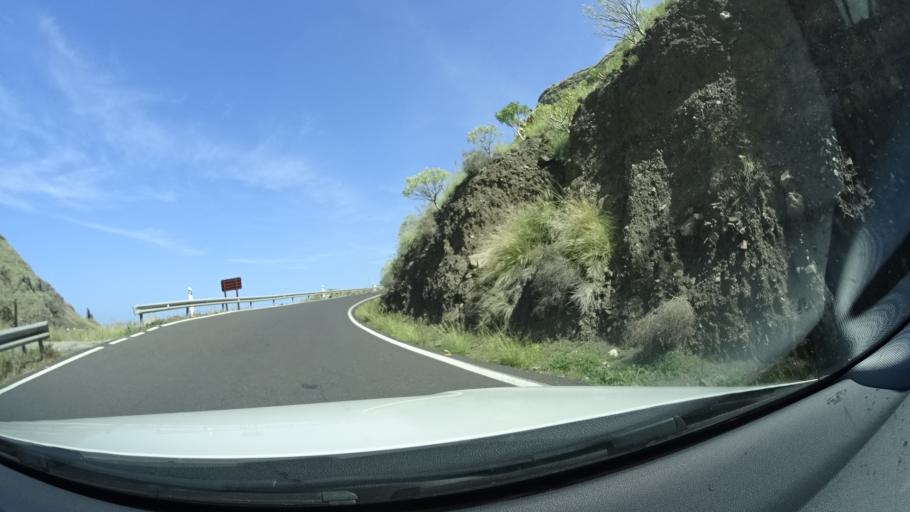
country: ES
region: Canary Islands
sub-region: Provincia de Las Palmas
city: Agaete
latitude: 28.0701
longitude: -15.7110
